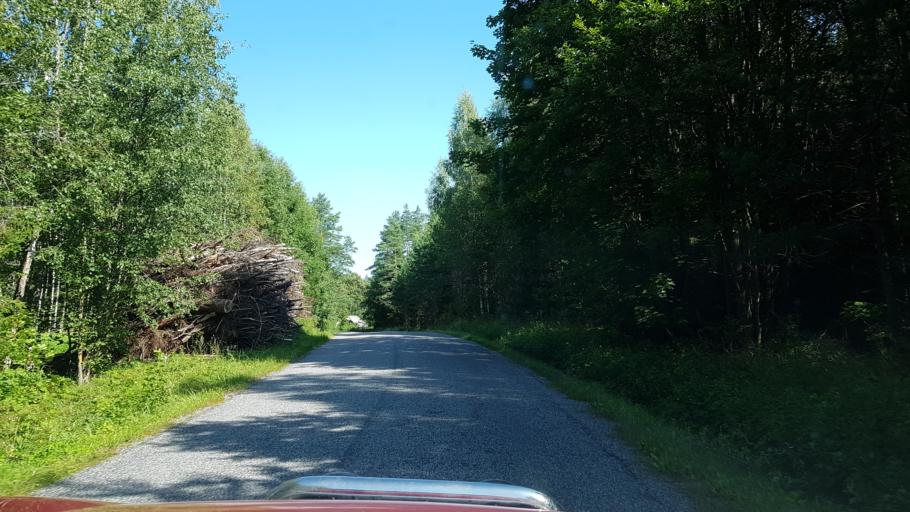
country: EE
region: Vorumaa
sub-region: Voru linn
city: Voru
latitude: 57.7130
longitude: 27.1949
